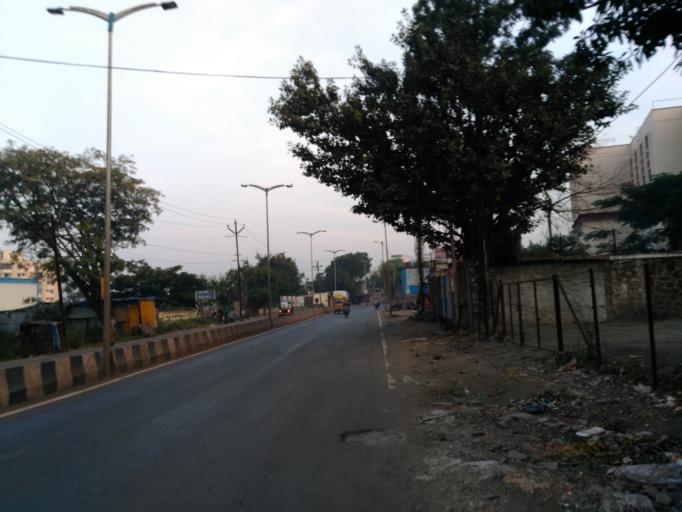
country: IN
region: Maharashtra
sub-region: Pune Division
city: Pune
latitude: 18.4531
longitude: 73.8910
